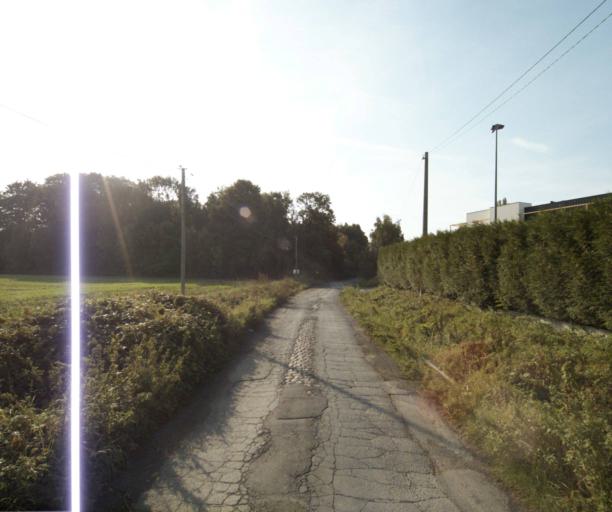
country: FR
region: Nord-Pas-de-Calais
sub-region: Departement du Nord
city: Lomme
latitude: 50.6556
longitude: 2.9930
